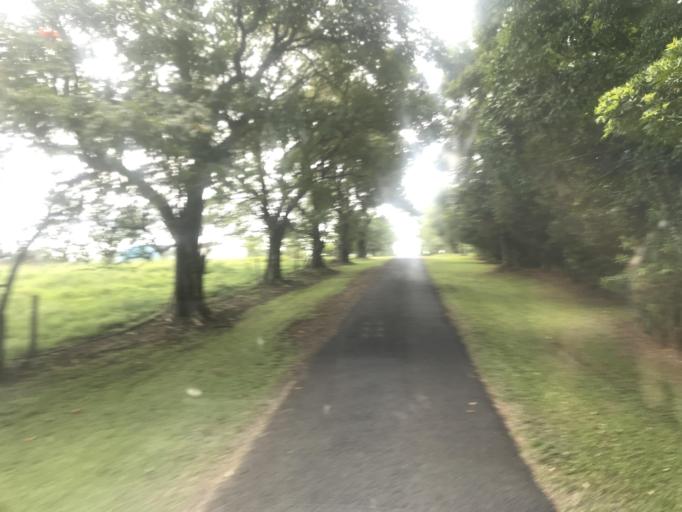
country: AU
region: Queensland
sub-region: Tablelands
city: Ravenshoe
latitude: -17.5546
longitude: 145.6933
